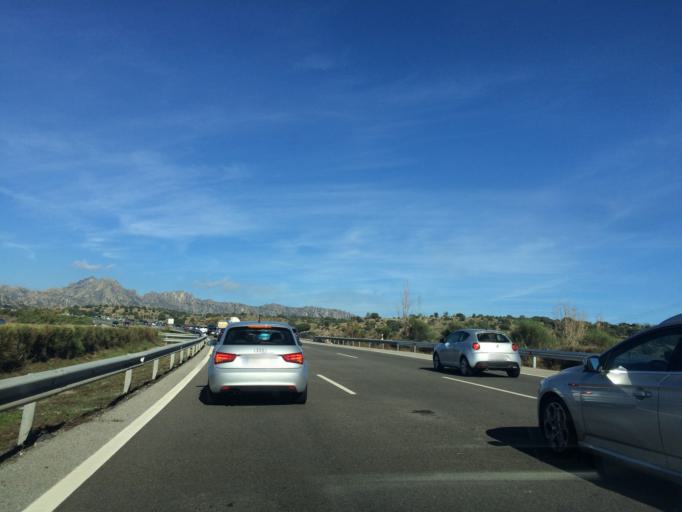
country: ES
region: Madrid
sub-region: Provincia de Madrid
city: Cabanillas de la Sierra
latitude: 40.8301
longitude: -3.6144
